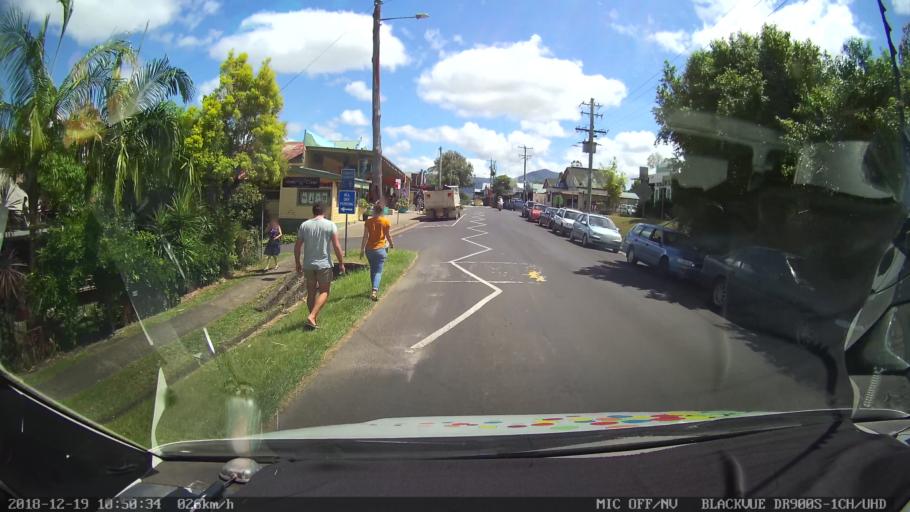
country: AU
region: New South Wales
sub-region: Lismore Municipality
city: Nimbin
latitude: -28.5972
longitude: 153.2228
